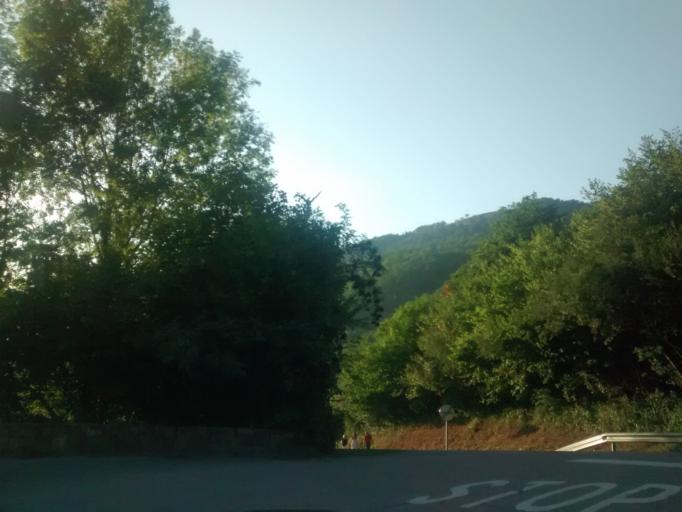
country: ES
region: Cantabria
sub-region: Provincia de Cantabria
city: Ruente
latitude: 43.1467
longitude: -4.1967
